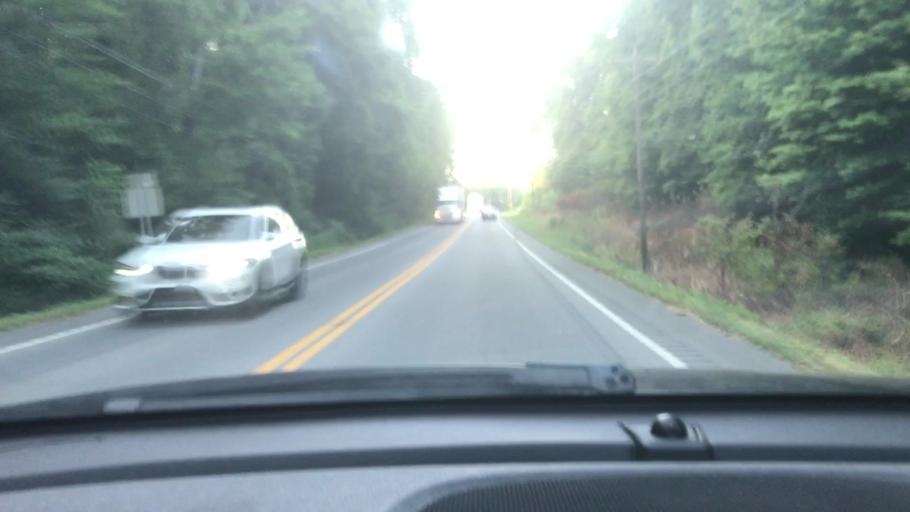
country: US
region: Tennessee
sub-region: Dickson County
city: Dickson
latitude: 36.1023
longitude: -87.3742
